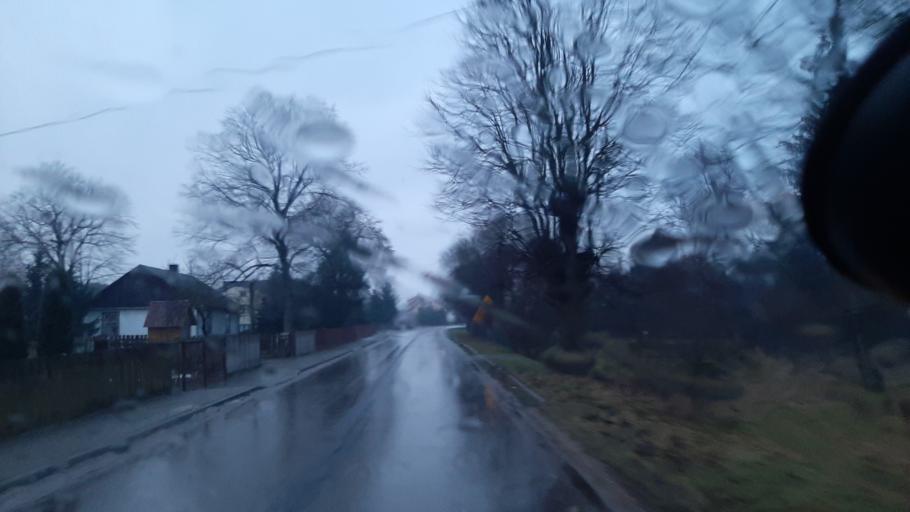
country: PL
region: Lublin Voivodeship
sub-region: Powiat lubartowski
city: Firlej
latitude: 51.5481
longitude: 22.5561
